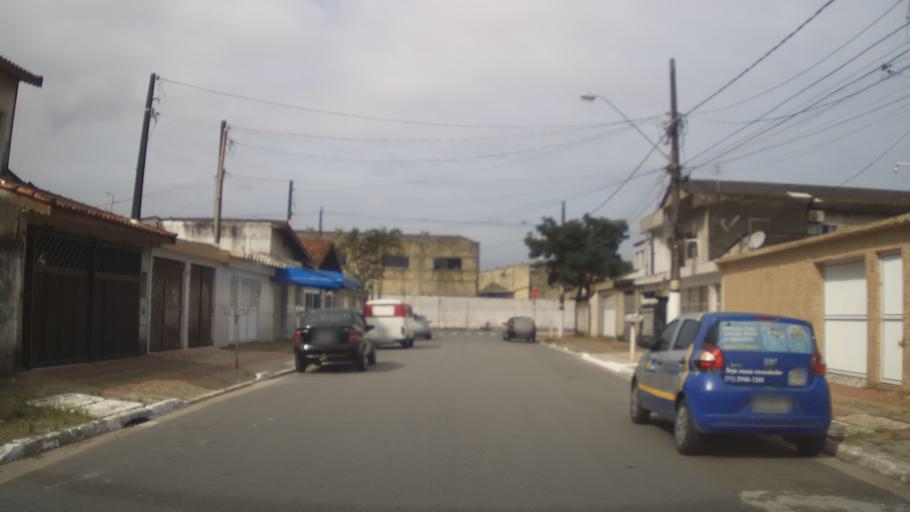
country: BR
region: Sao Paulo
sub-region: Praia Grande
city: Praia Grande
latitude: -24.0083
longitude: -46.4482
